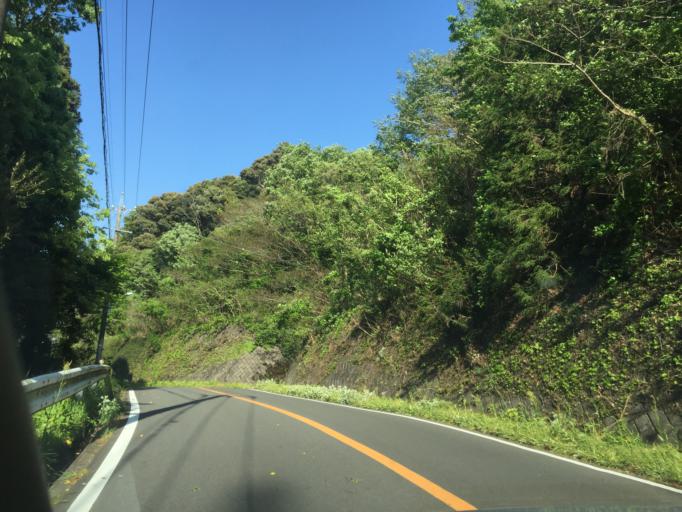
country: JP
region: Shizuoka
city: Kakegawa
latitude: 34.7705
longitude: 138.0540
